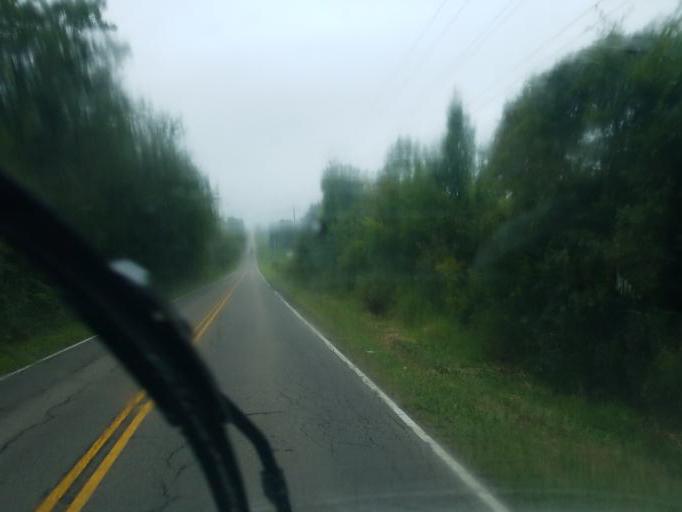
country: US
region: Ohio
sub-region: Licking County
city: Johnstown
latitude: 40.1587
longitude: -82.6558
